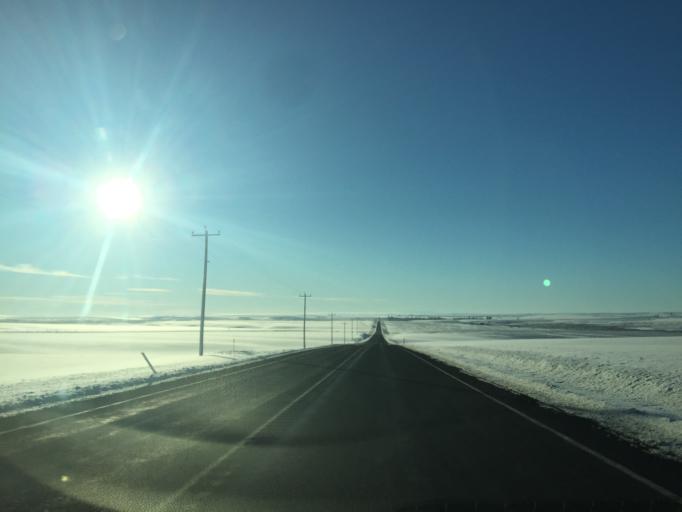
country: US
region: Washington
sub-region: Okanogan County
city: Coulee Dam
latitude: 47.7311
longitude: -118.8667
